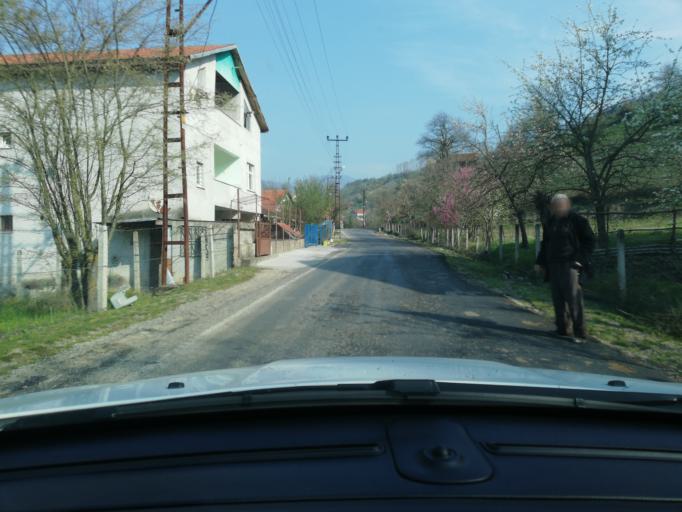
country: TR
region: Karabuk
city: Yenice
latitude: 41.2376
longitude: 32.3596
